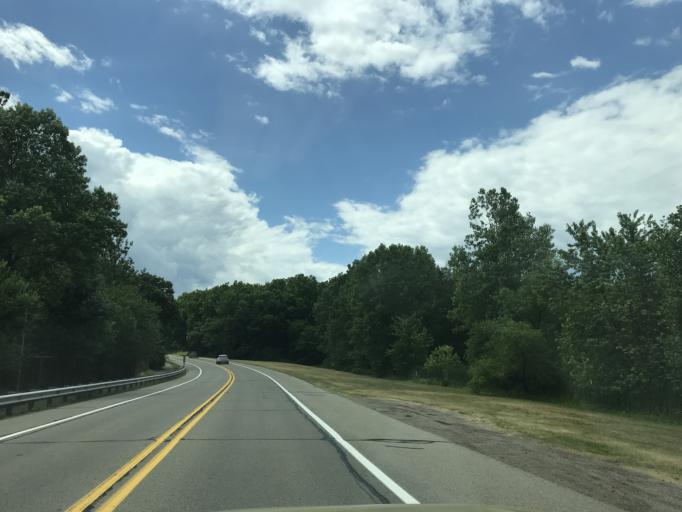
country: US
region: Michigan
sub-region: Wayne County
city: Redford
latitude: 42.3523
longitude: -83.3015
